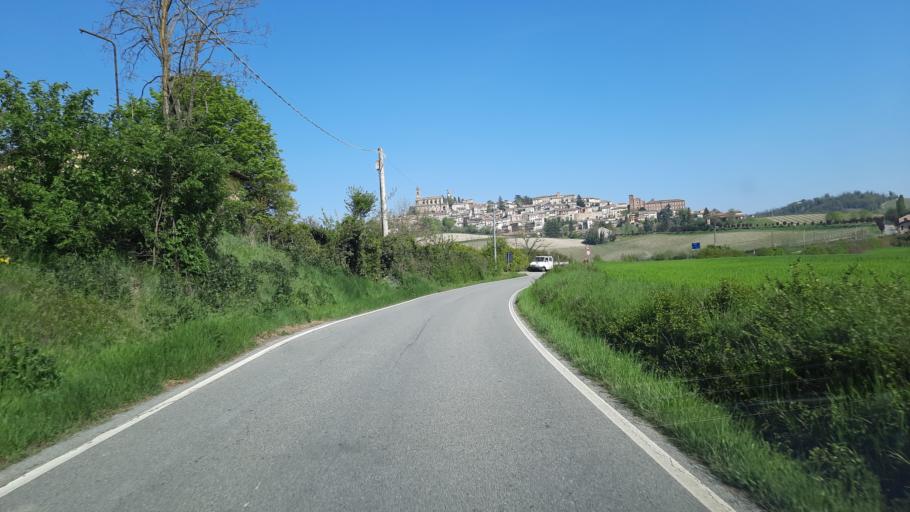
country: IT
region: Piedmont
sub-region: Provincia di Alessandria
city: Vignale Monferrato
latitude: 45.0117
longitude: 8.3826
